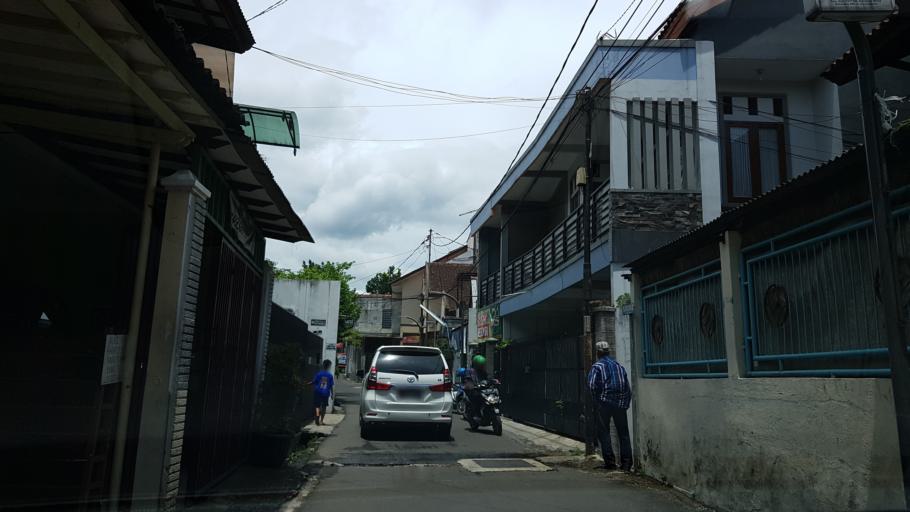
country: ID
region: West Java
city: Bandung
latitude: -6.9000
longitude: 107.6244
